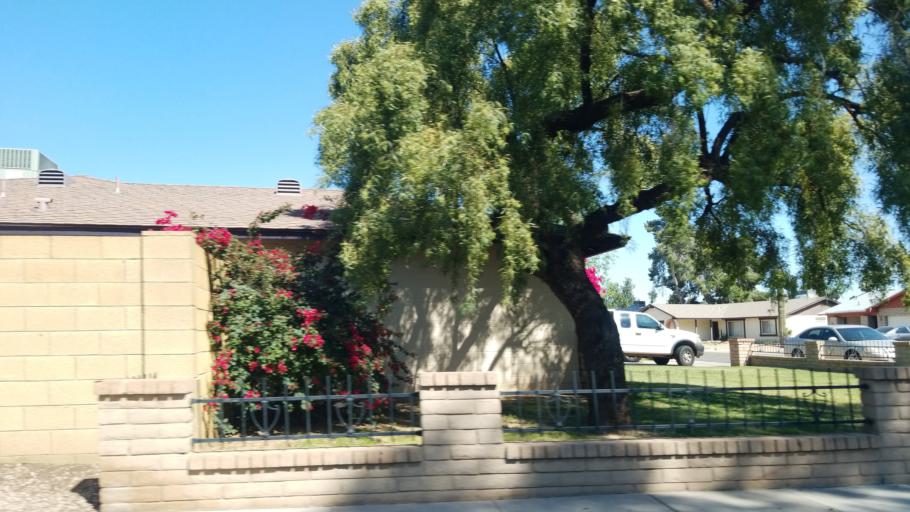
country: US
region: Arizona
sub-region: Maricopa County
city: Glendale
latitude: 33.5571
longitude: -112.1732
